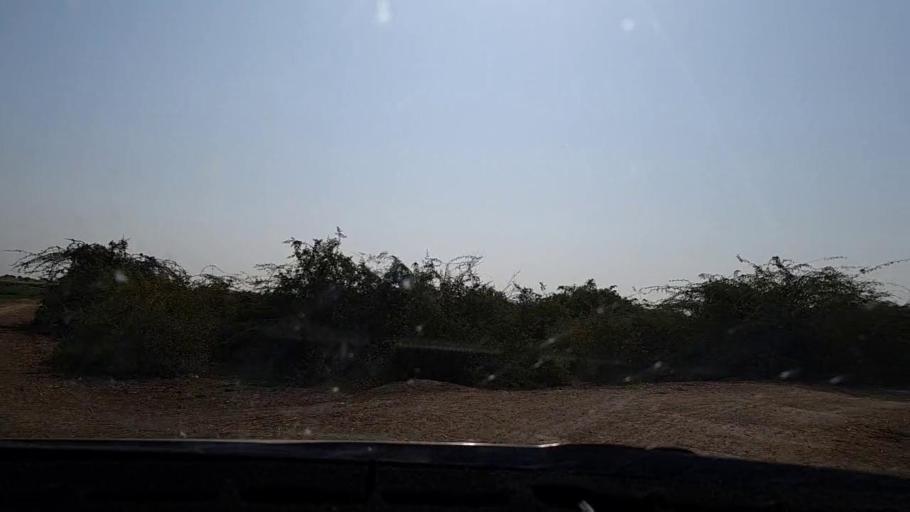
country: PK
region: Sindh
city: Tando Mittha Khan
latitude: 25.8115
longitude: 69.2963
